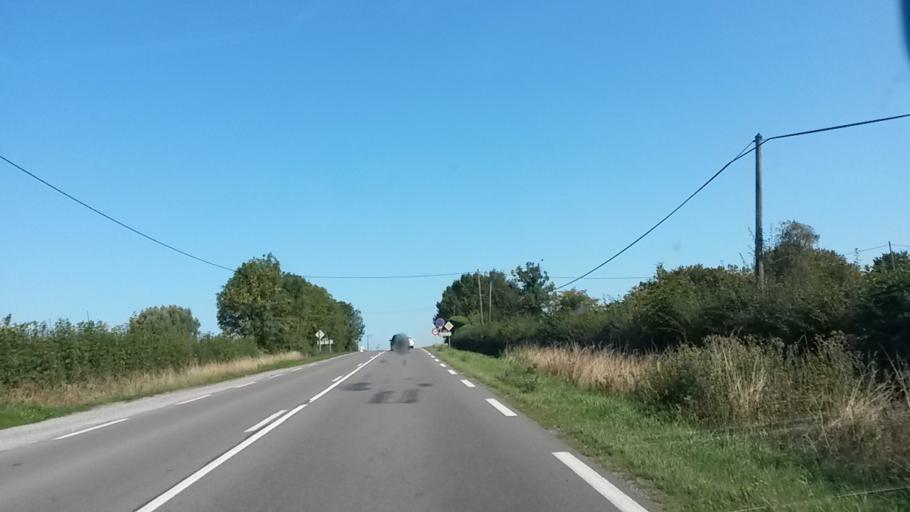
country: FR
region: Nord-Pas-de-Calais
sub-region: Departement du Nord
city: Avesnes-sur-Helpe
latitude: 50.1038
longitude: 3.9312
